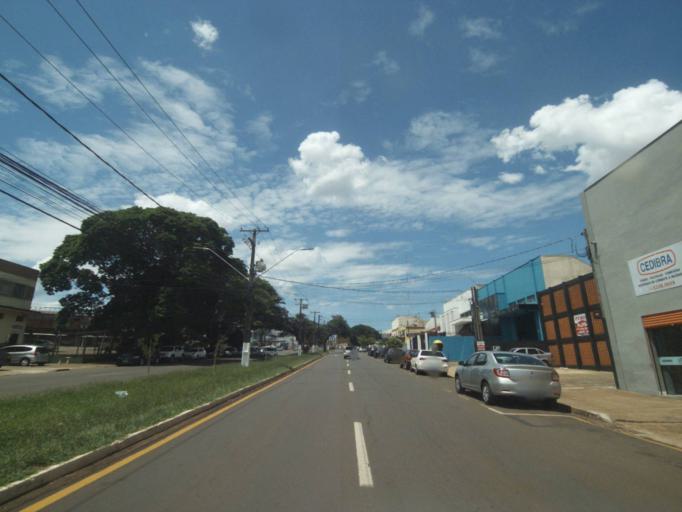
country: BR
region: Parana
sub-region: Londrina
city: Londrina
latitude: -23.3006
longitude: -51.1937
